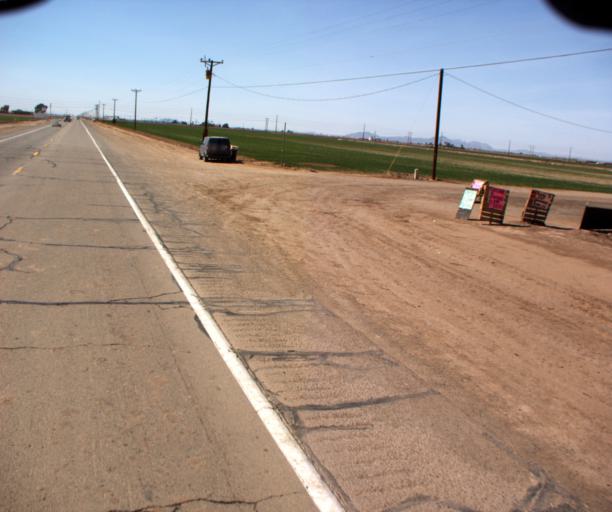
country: US
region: Arizona
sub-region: Yuma County
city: Fortuna Foothills
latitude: 32.6995
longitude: -114.4632
